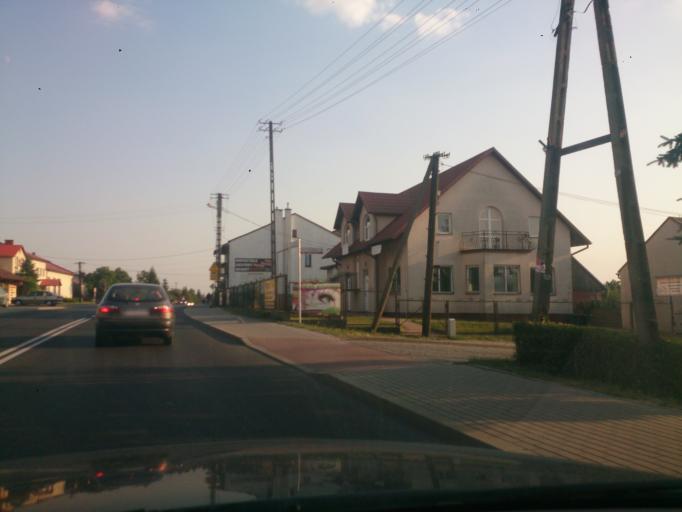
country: PL
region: Subcarpathian Voivodeship
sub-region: Powiat kolbuszowski
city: Majdan Krolewski
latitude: 50.3755
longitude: 21.7459
